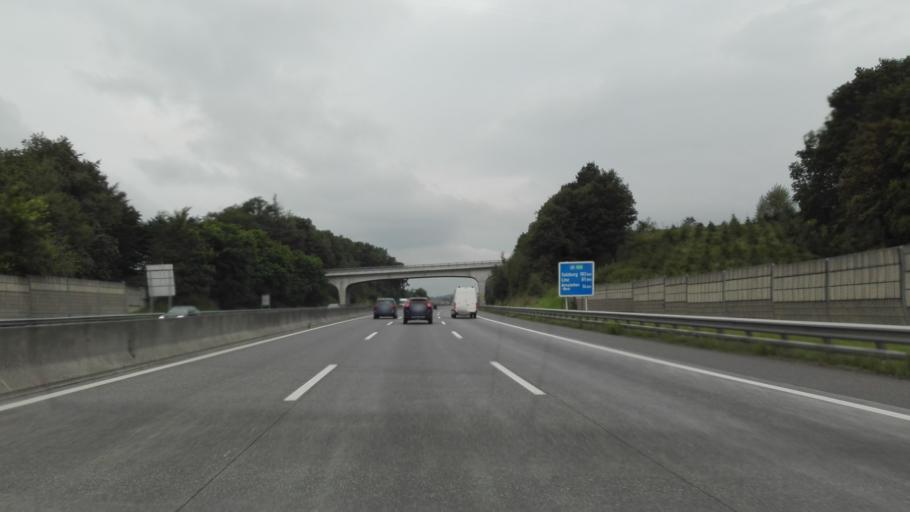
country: AT
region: Lower Austria
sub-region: Politischer Bezirk Melk
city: Blindenmarkt
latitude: 48.1294
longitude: 15.0057
